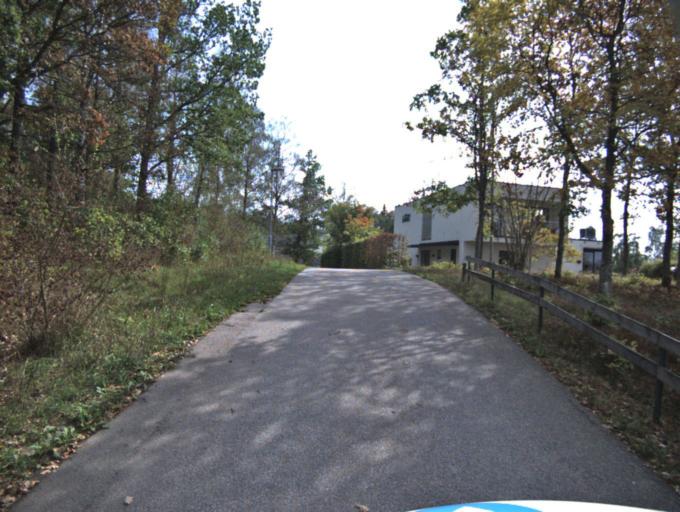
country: SE
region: Vaestra Goetaland
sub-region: Ulricehamns Kommun
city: Ulricehamn
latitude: 57.7785
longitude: 13.4093
